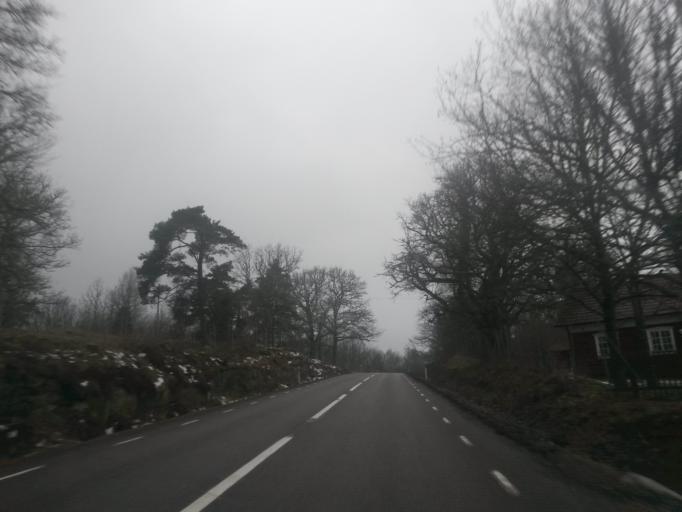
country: SE
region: Vaestra Goetaland
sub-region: Alingsas Kommun
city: Sollebrunn
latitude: 58.1386
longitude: 12.4253
